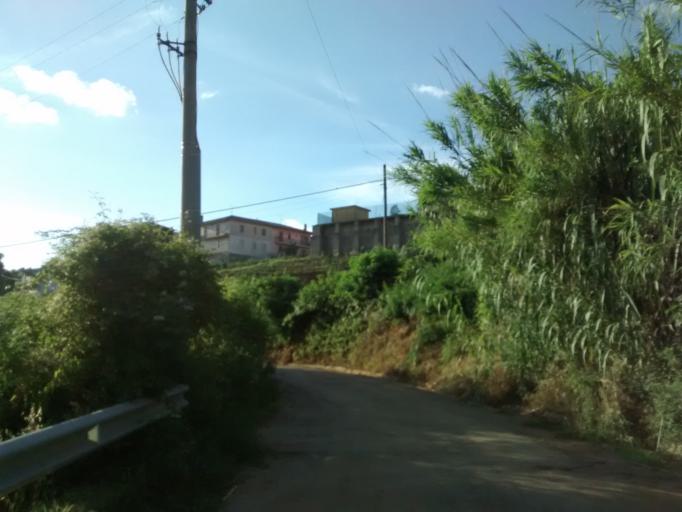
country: IT
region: Calabria
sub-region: Provincia di Catanzaro
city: Cortale
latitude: 38.8866
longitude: 16.4077
